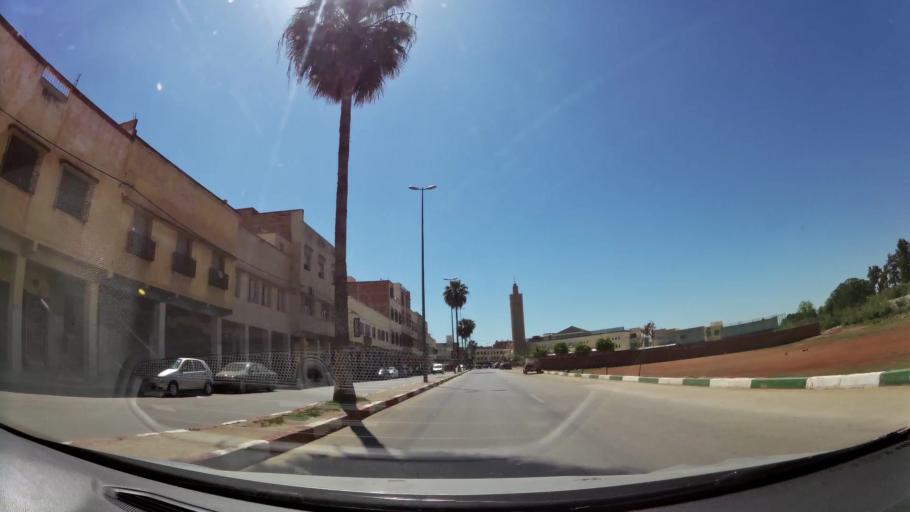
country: MA
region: Meknes-Tafilalet
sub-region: Meknes
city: Meknes
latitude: 33.8700
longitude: -5.5525
